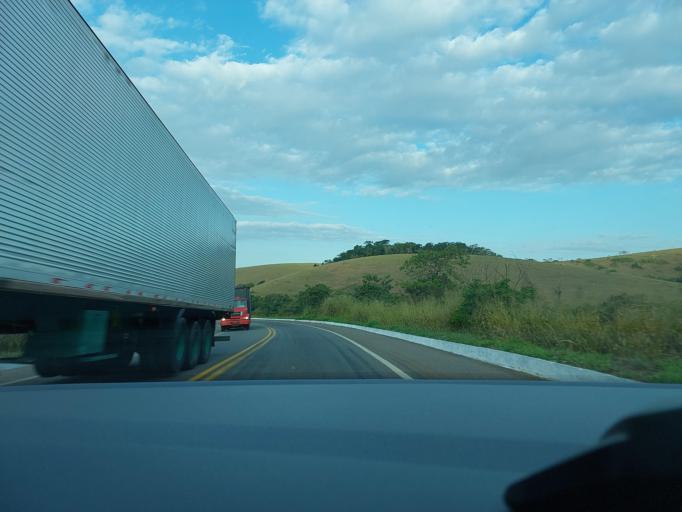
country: BR
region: Minas Gerais
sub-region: Muriae
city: Muriae
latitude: -21.1383
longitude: -42.3078
